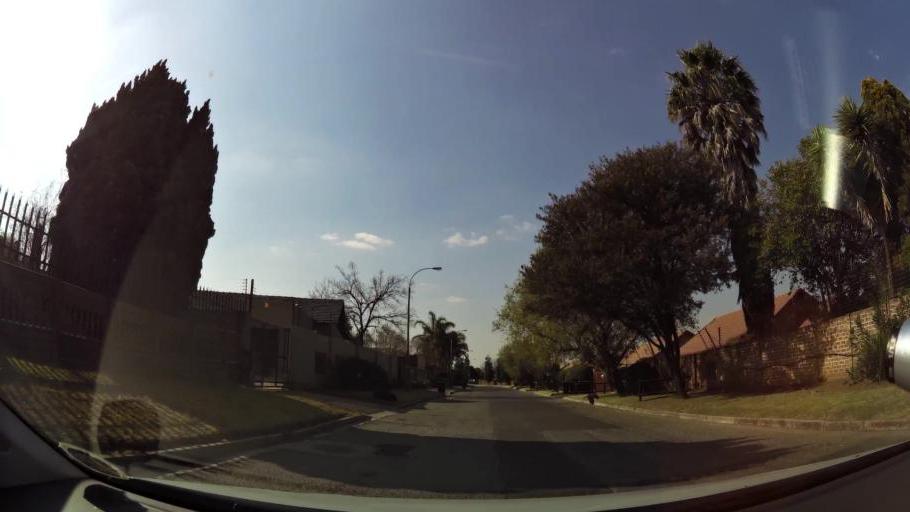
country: ZA
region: Gauteng
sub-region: City of Johannesburg Metropolitan Municipality
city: Modderfontein
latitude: -26.0971
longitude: 28.2134
